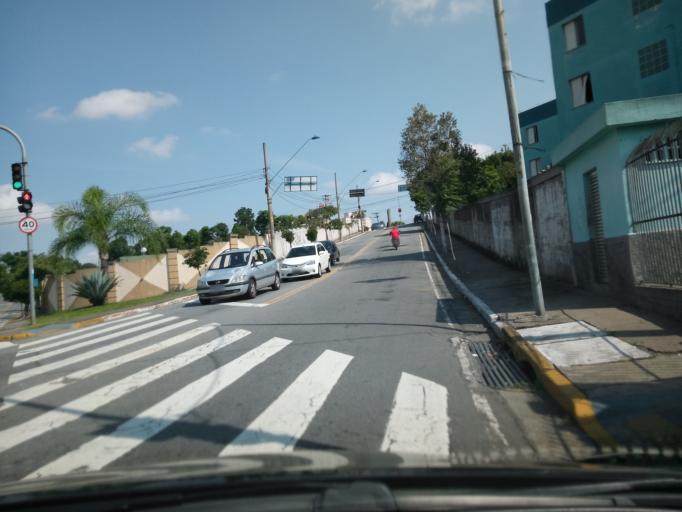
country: BR
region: Sao Paulo
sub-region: Sao Caetano Do Sul
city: Sao Caetano do Sul
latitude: -23.6370
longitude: -46.5749
